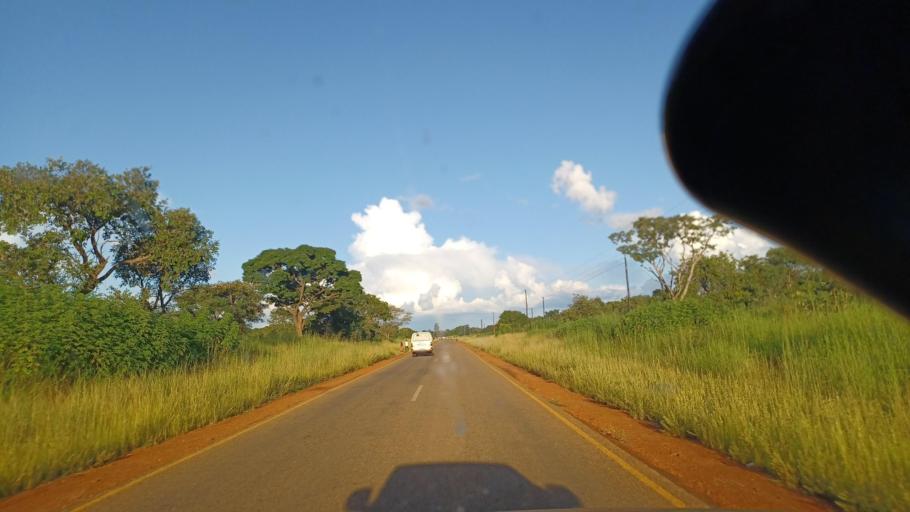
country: ZM
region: North-Western
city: Kalengwa
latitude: -13.1419
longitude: 25.0251
